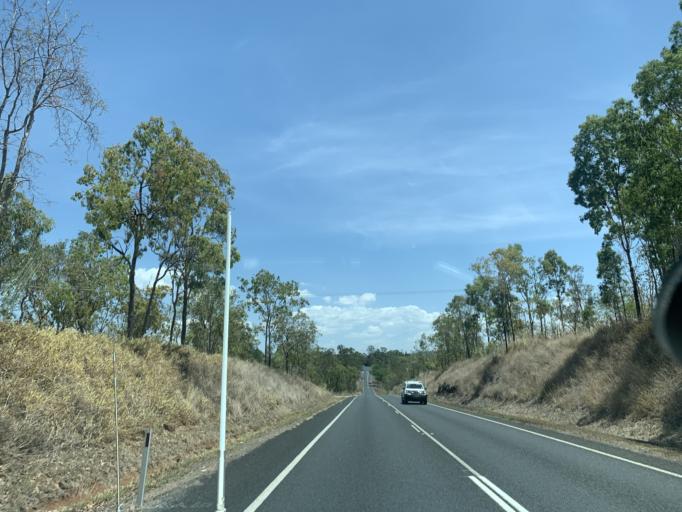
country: AU
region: Queensland
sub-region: Tablelands
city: Mareeba
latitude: -16.9623
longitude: 145.5383
